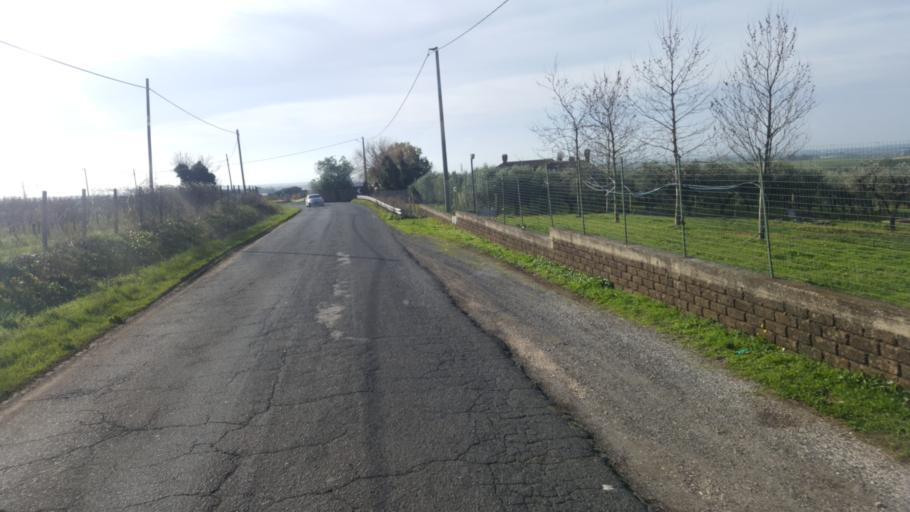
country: IT
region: Latium
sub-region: Citta metropolitana di Roma Capitale
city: Mantiglia di Ardea
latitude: 41.6643
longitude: 12.6307
